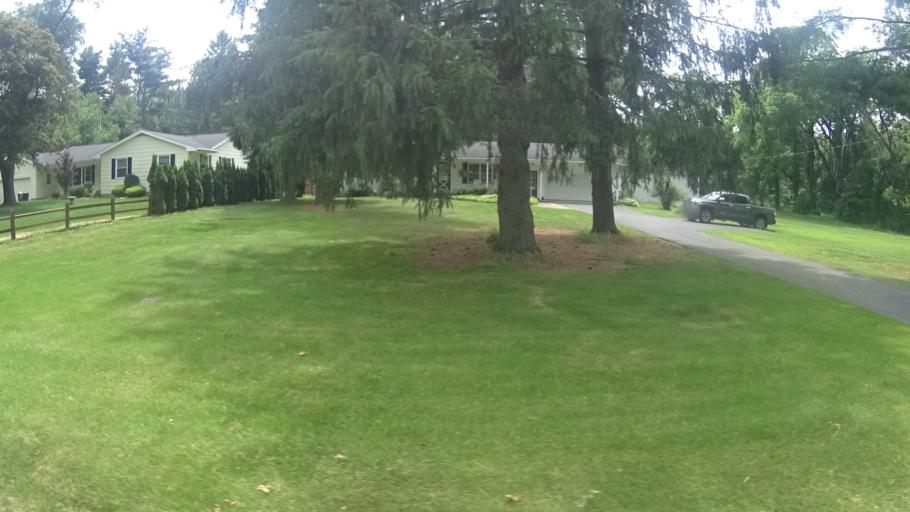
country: US
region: Ohio
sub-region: Erie County
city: Milan
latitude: 41.3061
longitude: -82.6126
